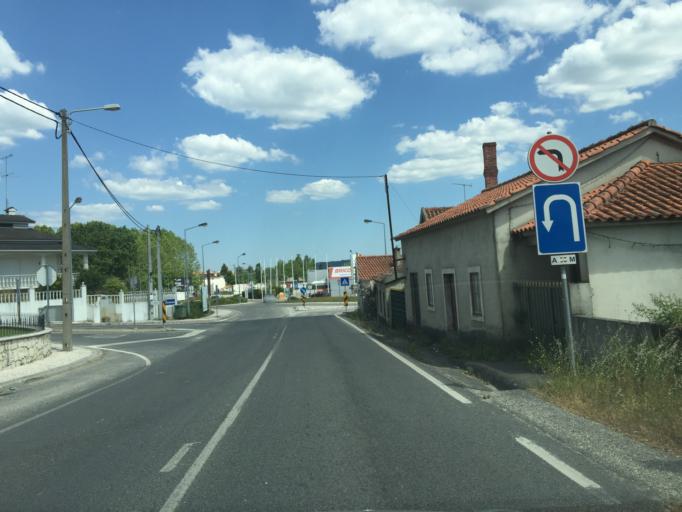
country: PT
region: Santarem
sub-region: Ourem
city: Ourem
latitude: 39.6542
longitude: -8.5929
